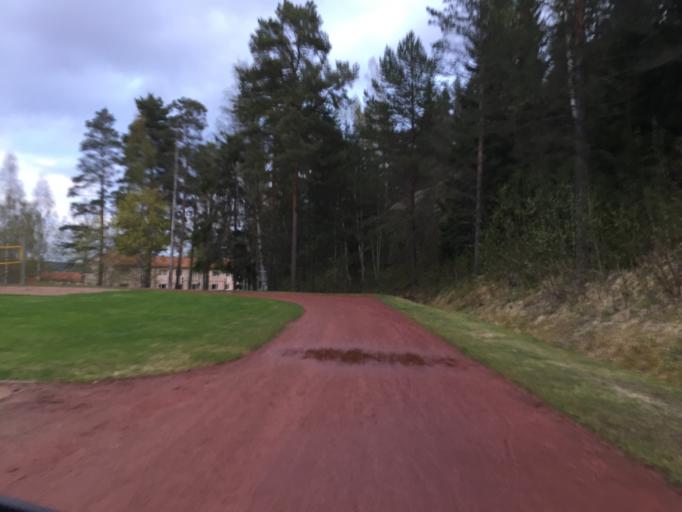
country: SE
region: Dalarna
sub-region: Ludvika Kommun
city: Ludvika
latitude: 60.1402
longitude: 15.1899
